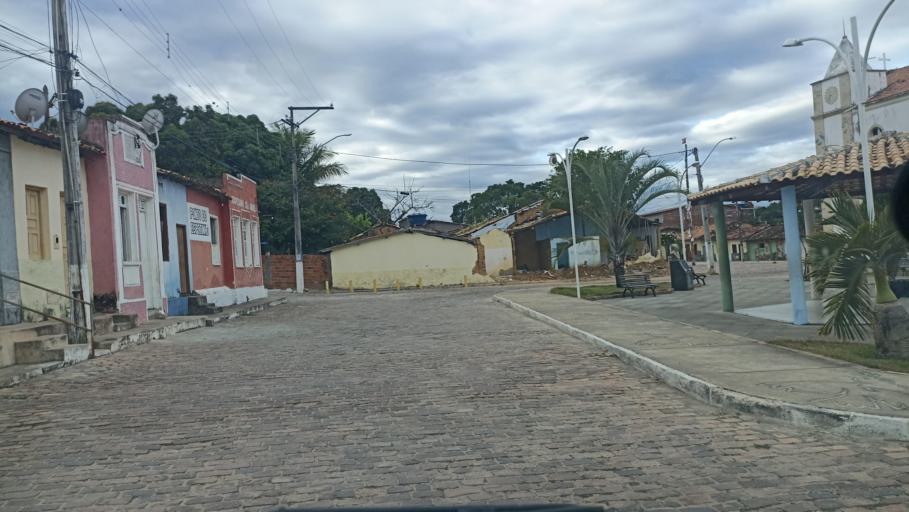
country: BR
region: Bahia
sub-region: Andarai
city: Vera Cruz
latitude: -12.8112
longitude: -41.3321
